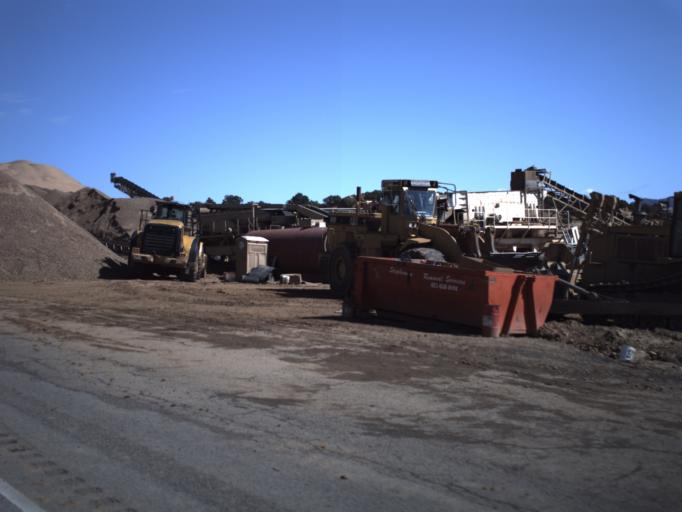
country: US
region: Utah
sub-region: Carbon County
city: East Carbon City
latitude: 39.3982
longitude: -110.4212
